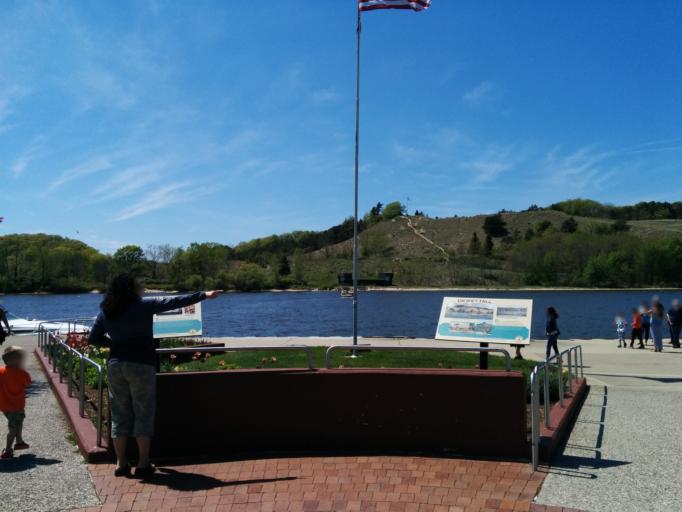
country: US
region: Michigan
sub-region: Ottawa County
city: Grand Haven
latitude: 43.0651
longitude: -86.2347
